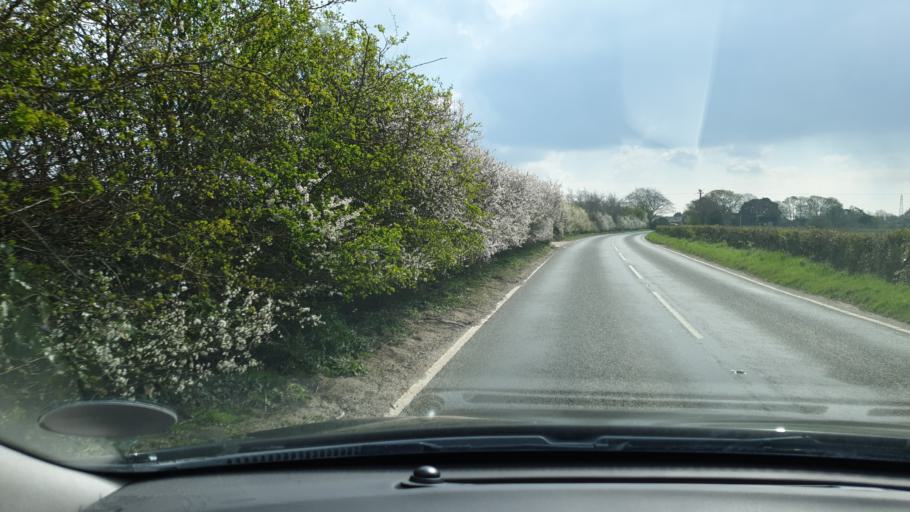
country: GB
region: England
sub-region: Essex
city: Alresford
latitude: 51.9157
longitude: 0.9940
